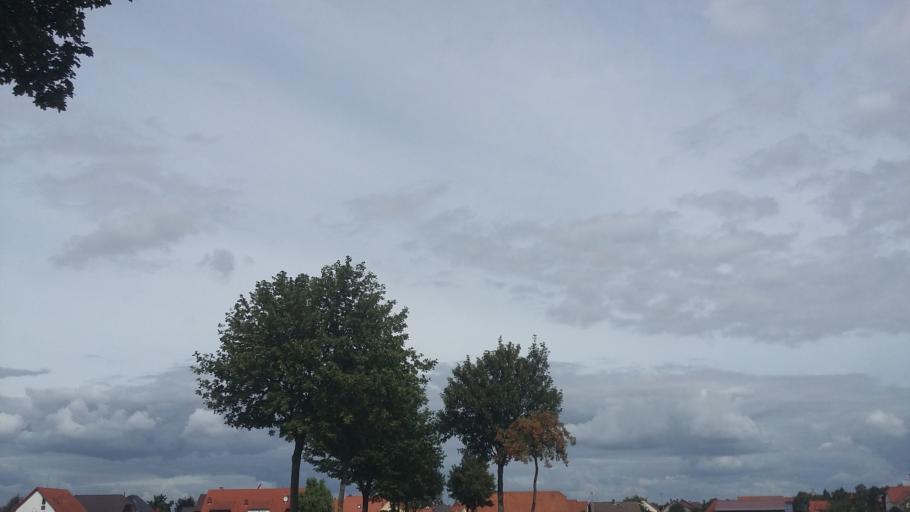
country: DE
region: Lower Saxony
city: Harsum
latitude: 52.2018
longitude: 10.0082
